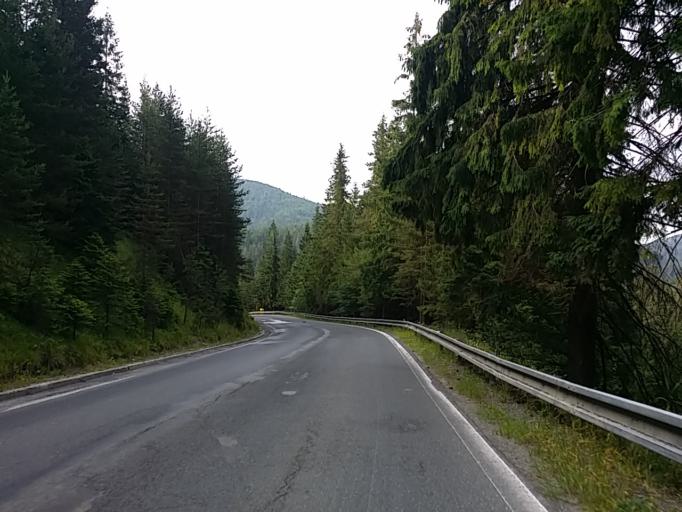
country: SK
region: Kosicky
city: Dobsina
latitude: 48.8881
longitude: 20.2394
